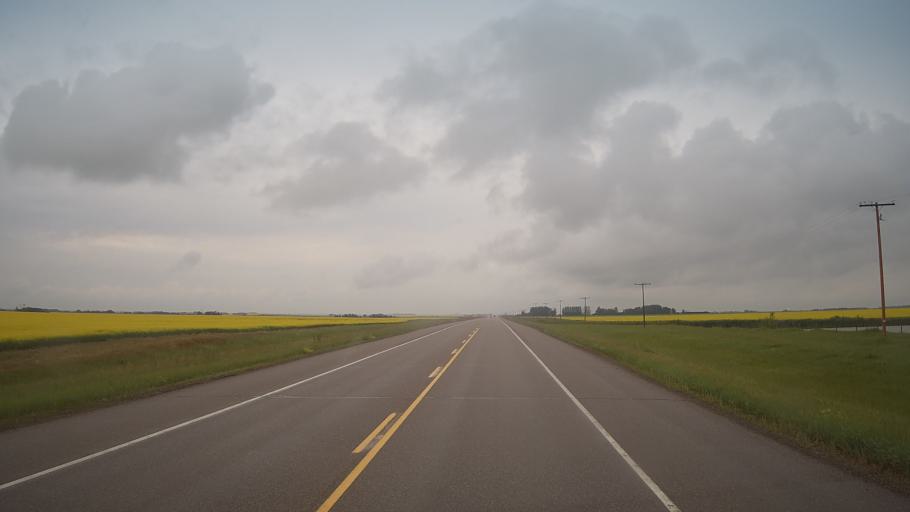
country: CA
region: Saskatchewan
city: Unity
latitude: 52.4350
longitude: -108.9542
